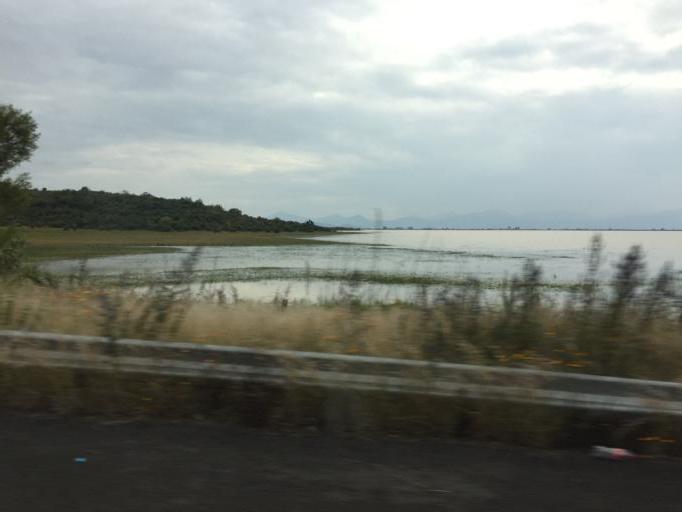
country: MX
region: Michoacan
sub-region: Puruandiro
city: San Lorenzo
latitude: 19.9454
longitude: -101.6363
